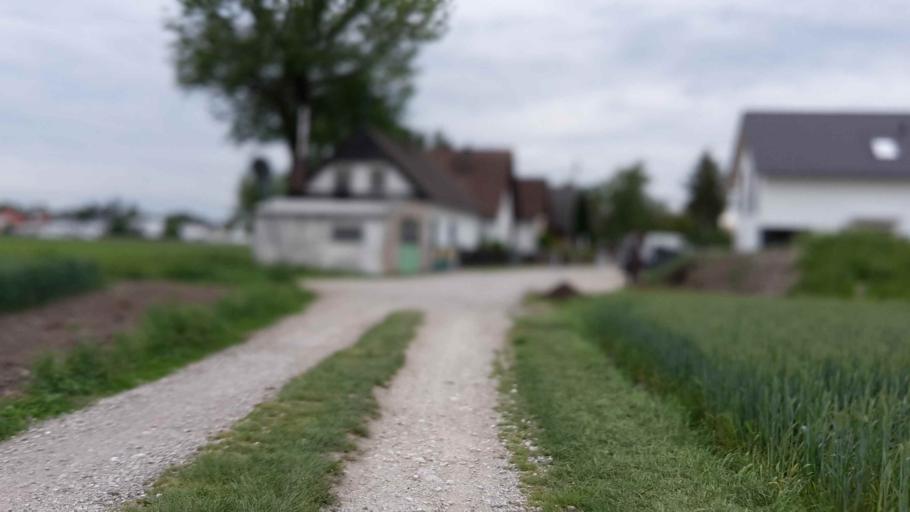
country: DE
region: Bavaria
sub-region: Upper Bavaria
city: Grobenzell
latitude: 48.1842
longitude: 11.4183
